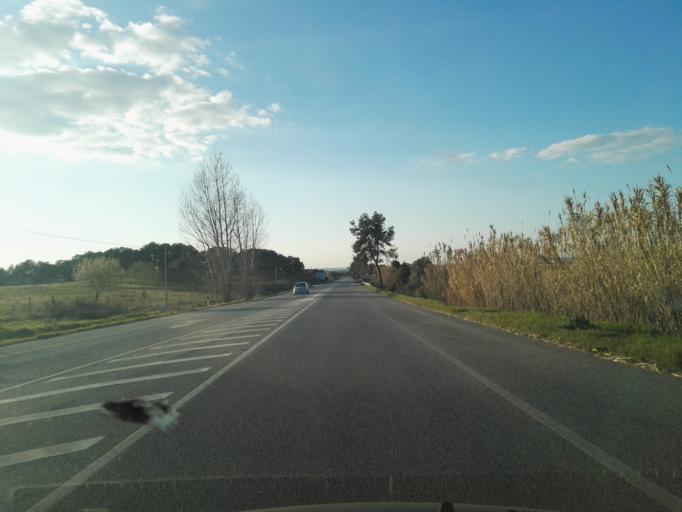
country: PT
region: Evora
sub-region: Arraiolos
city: Arraiolos
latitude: 38.6054
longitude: -8.0539
